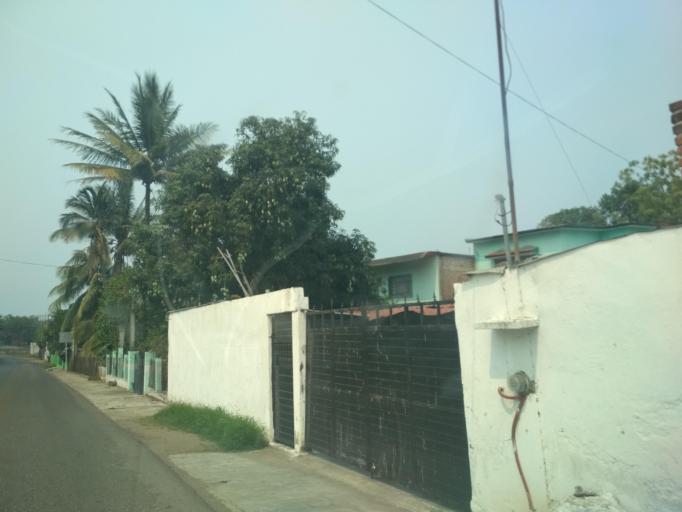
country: MX
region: Veracruz
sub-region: Veracruz
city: Delfino Victoria (Santa Fe)
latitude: 19.2076
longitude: -96.3205
